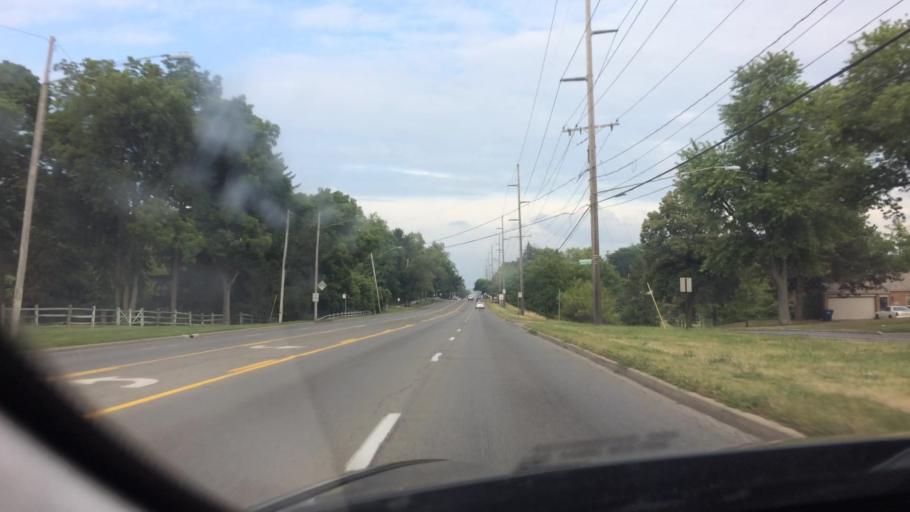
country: US
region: Ohio
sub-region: Lucas County
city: Ottawa Hills
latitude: 41.6527
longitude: -83.6391
